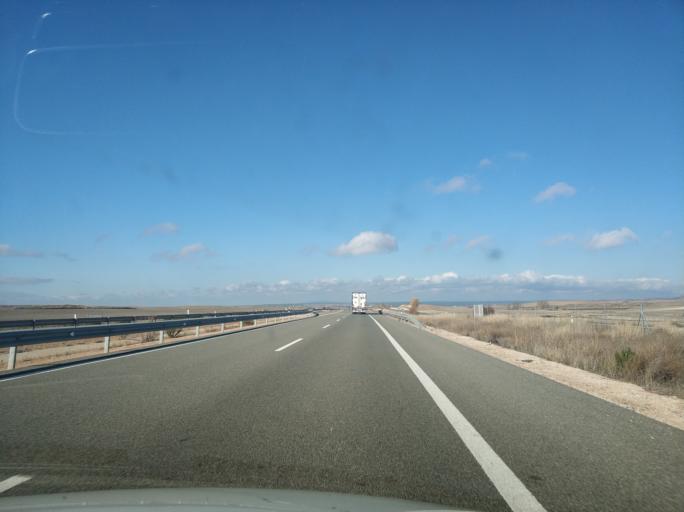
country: ES
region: Castille and Leon
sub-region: Provincia de Soria
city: Coscurita
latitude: 41.4031
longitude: -2.4789
